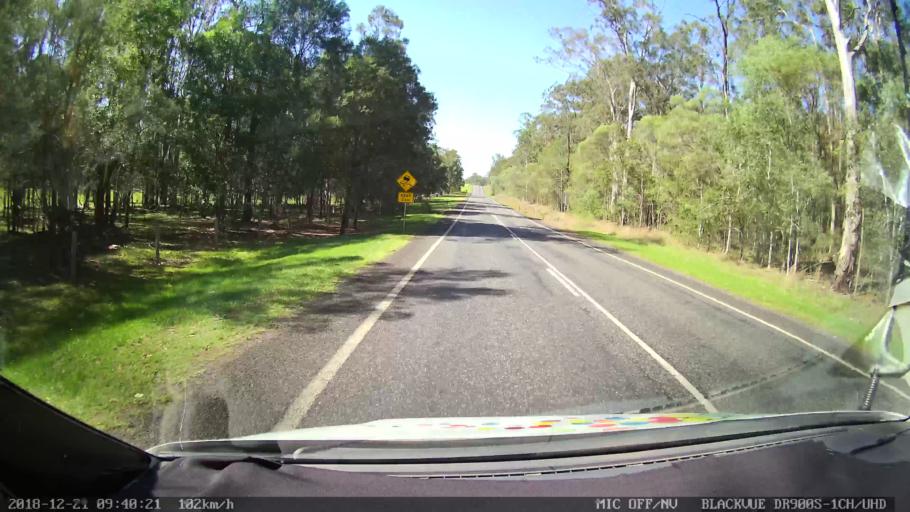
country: AU
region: New South Wales
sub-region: Clarence Valley
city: Grafton
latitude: -29.5713
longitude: 152.9637
